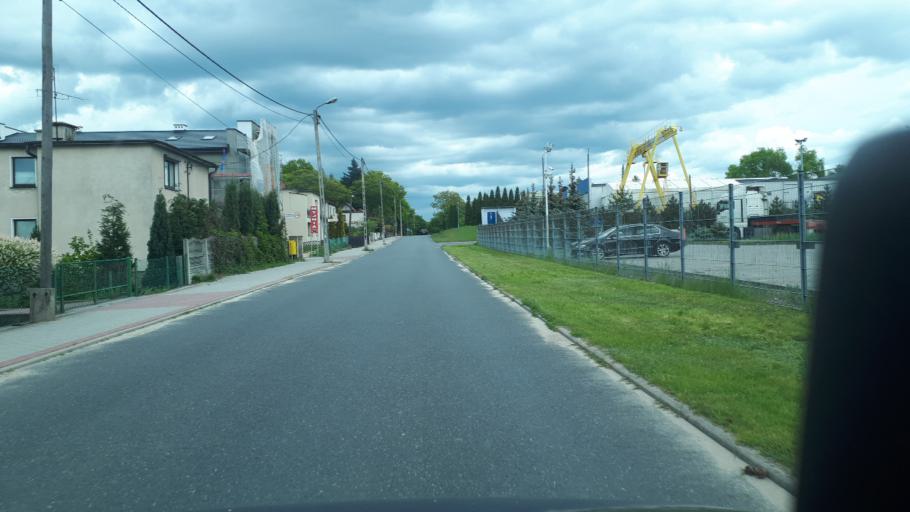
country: PL
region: Greater Poland Voivodeship
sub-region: Powiat ostrzeszowski
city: Ostrzeszow
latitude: 51.4231
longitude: 17.9186
